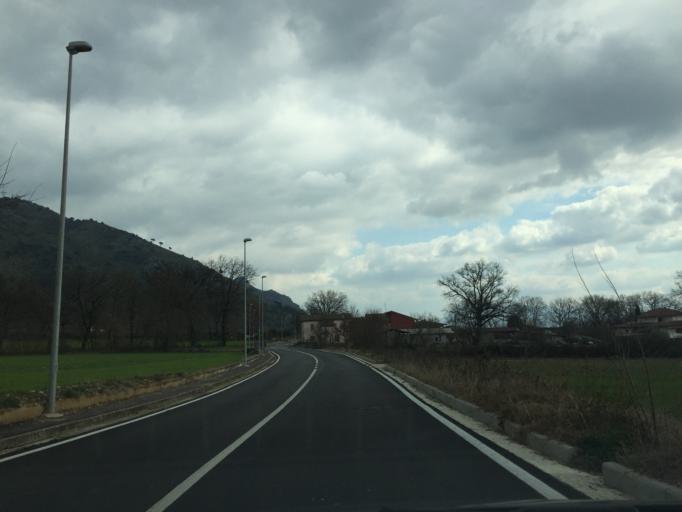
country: IT
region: Latium
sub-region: Provincia di Frosinone
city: Villa Santa Lucia
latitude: 41.4958
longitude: 13.7698
